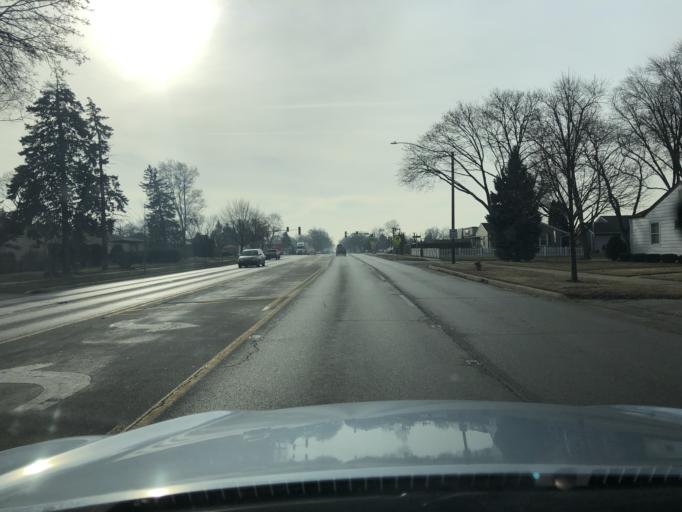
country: US
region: Illinois
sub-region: Cook County
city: Des Plaines
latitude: 42.0323
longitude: -87.9091
